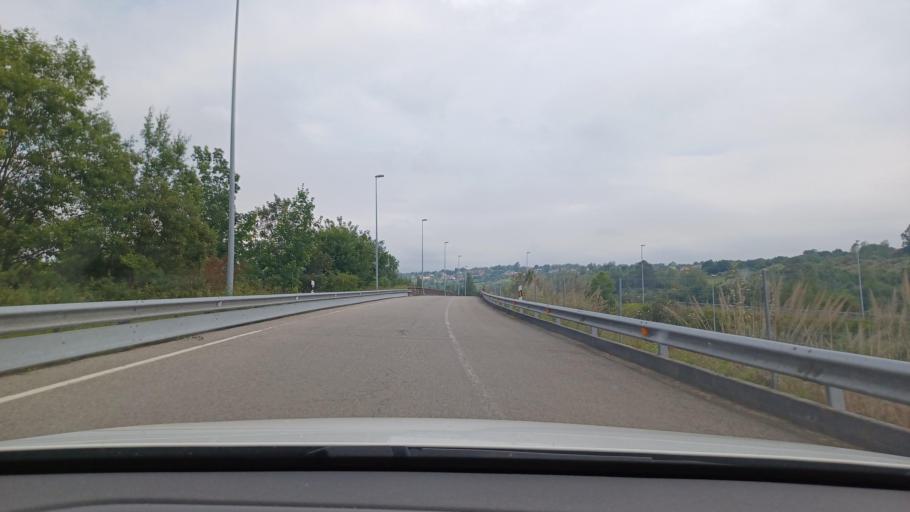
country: ES
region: Asturias
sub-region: Province of Asturias
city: Oviedo
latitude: 43.3437
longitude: -5.8672
